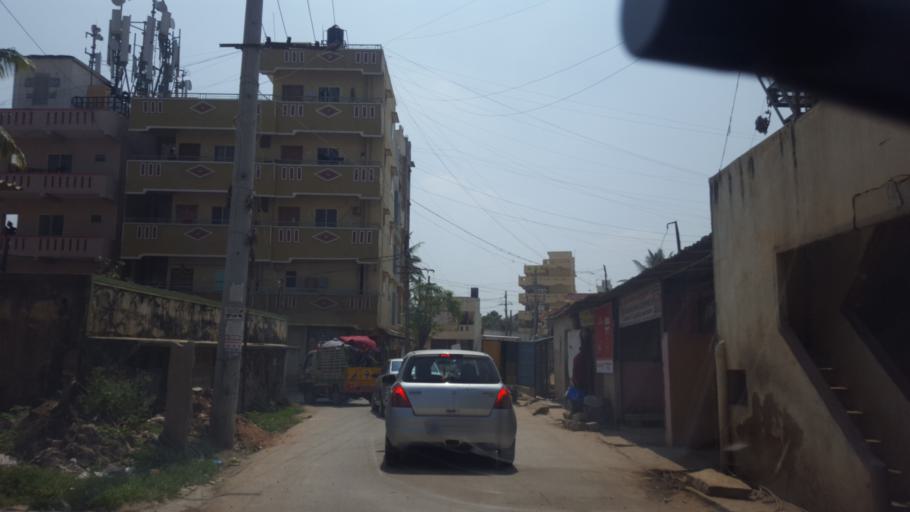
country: IN
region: Karnataka
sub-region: Bangalore Urban
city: Bangalore
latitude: 12.9358
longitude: 77.7057
